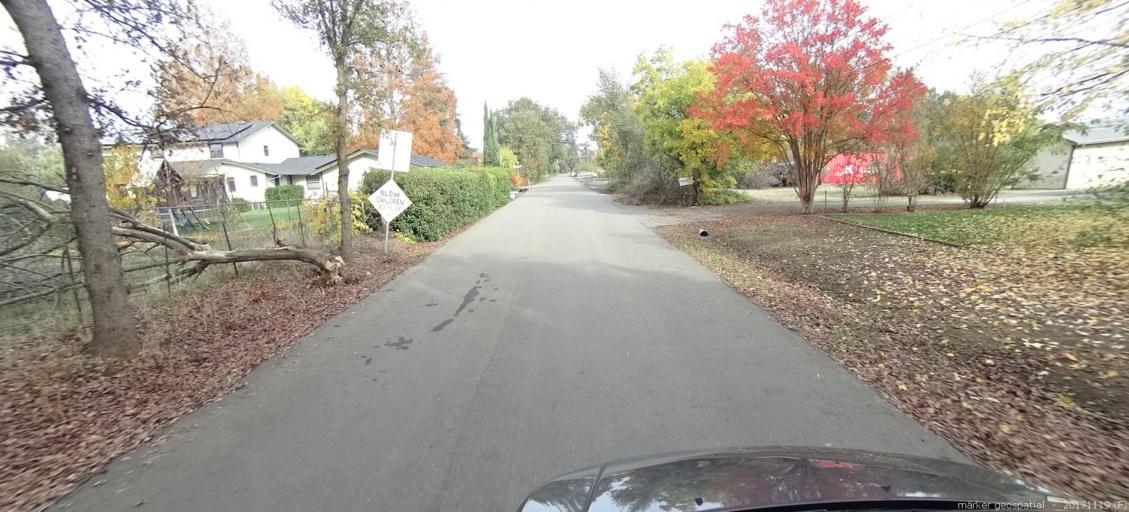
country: US
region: California
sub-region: Shasta County
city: Redding
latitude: 40.5235
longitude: -122.3394
